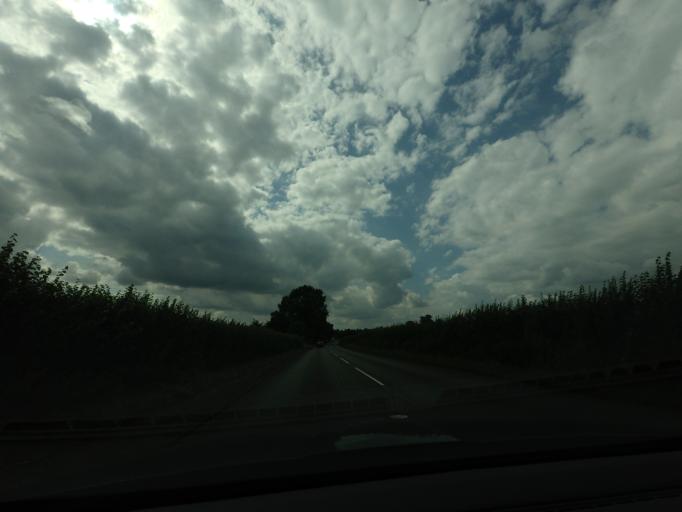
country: GB
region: England
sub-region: Staffordshire
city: Brewood
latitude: 52.6940
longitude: -2.1496
